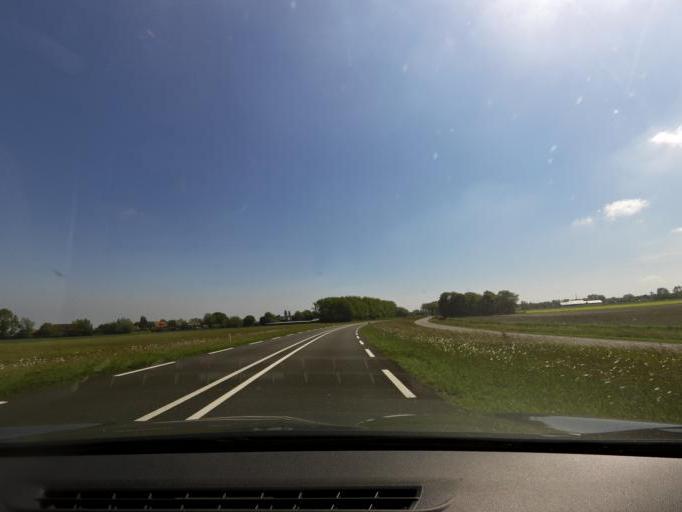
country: NL
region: South Holland
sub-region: Gemeente Hellevoetsluis
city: Nieuw-Helvoet
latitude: 51.8437
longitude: 4.0953
